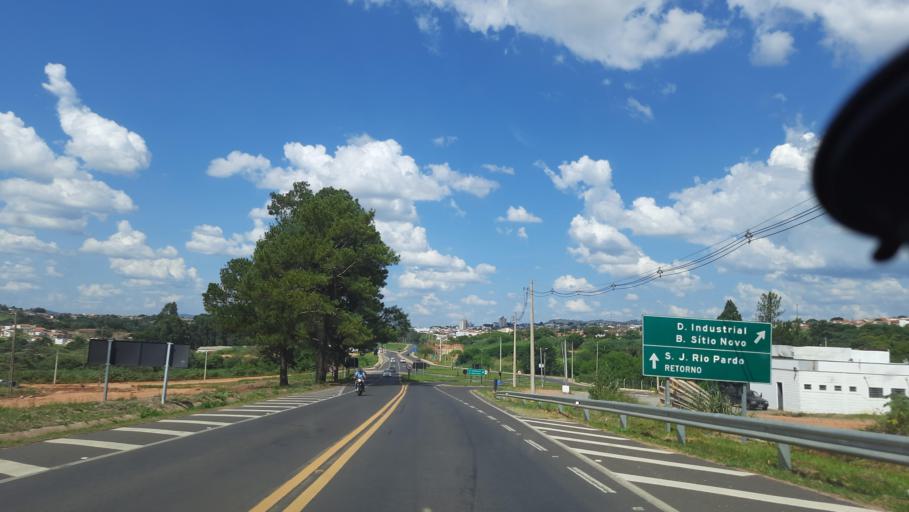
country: BR
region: Sao Paulo
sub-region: Sao Jose Do Rio Pardo
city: Sao Jose do Rio Pardo
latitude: -21.6037
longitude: -46.9171
